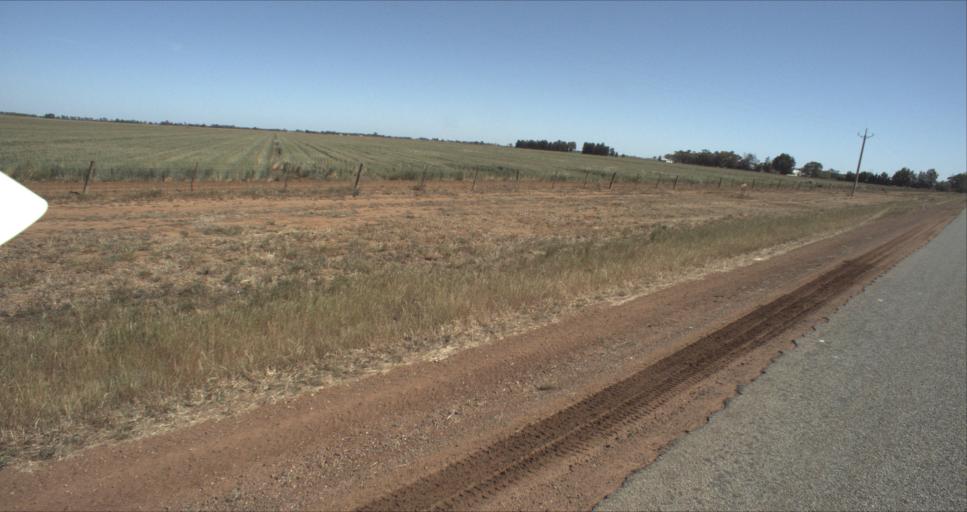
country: AU
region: New South Wales
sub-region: Leeton
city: Leeton
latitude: -34.5491
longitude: 146.3150
